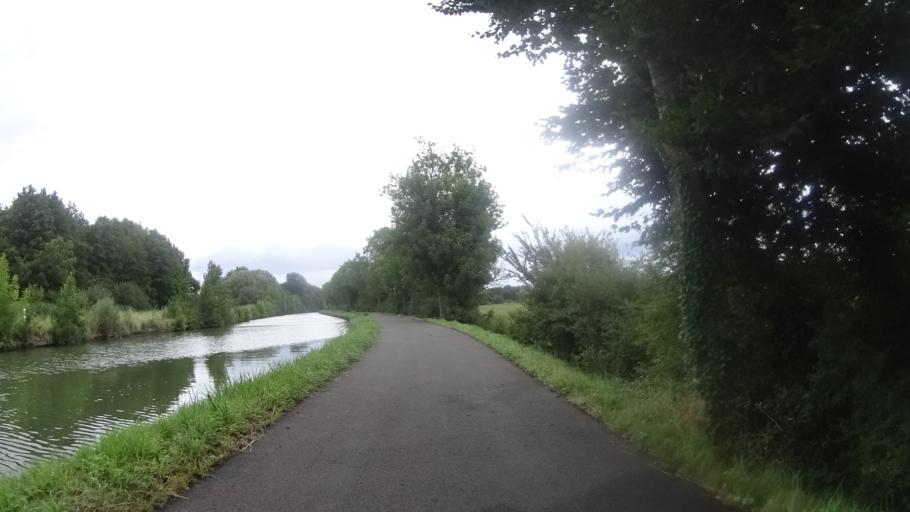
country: FR
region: Lorraine
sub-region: Departement de Meurthe-et-Moselle
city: Einville-au-Jard
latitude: 48.6767
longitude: 6.5626
